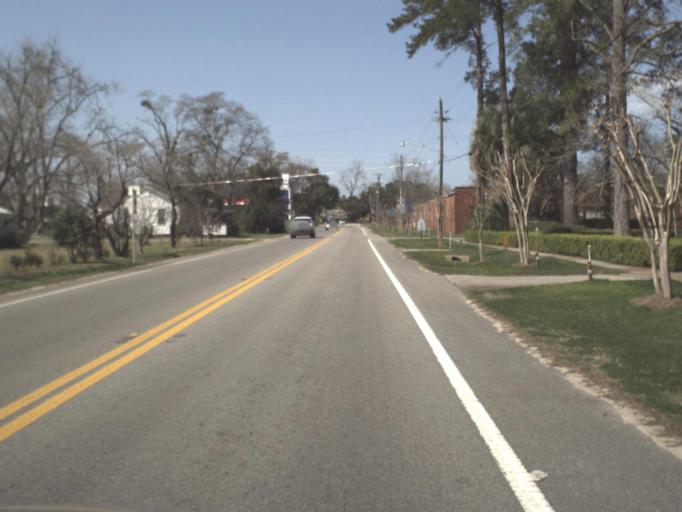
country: US
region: Florida
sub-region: Gadsden County
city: Gretna
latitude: 30.5701
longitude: -84.7407
